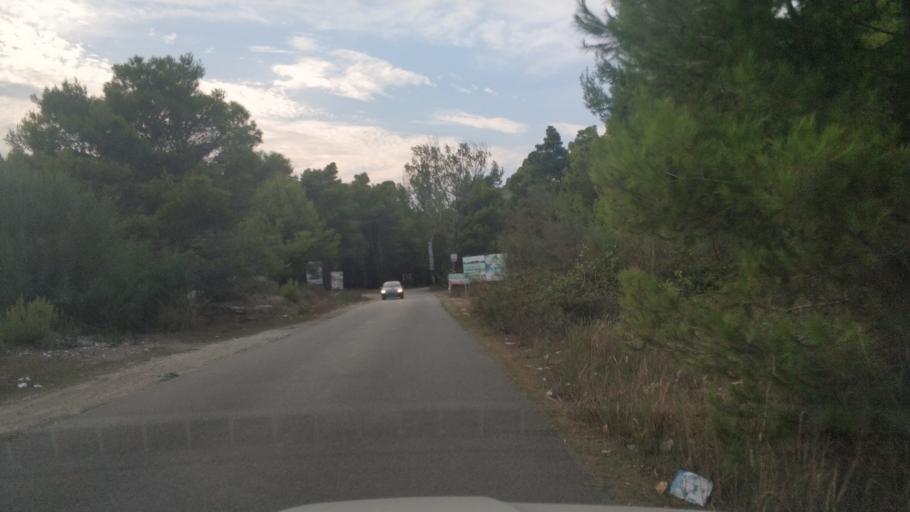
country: AL
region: Vlore
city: Vlore
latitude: 40.4915
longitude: 19.4373
